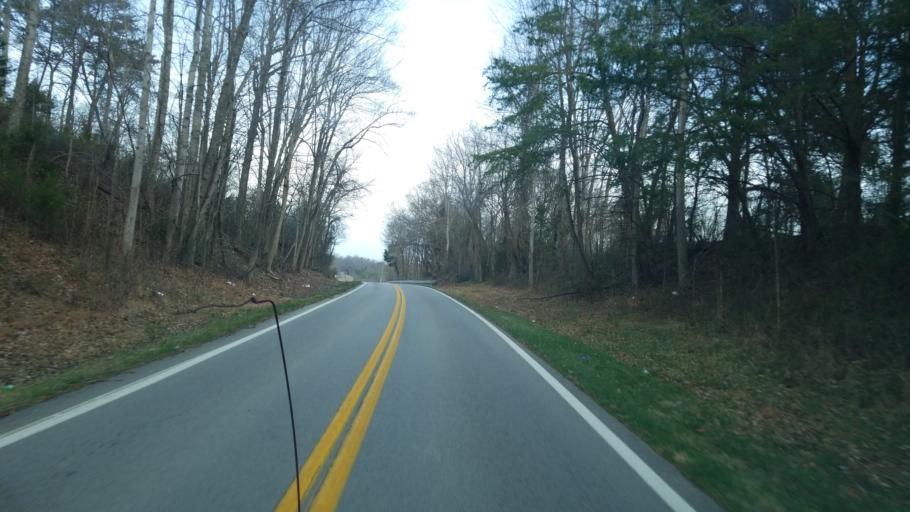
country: US
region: Kentucky
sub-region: Clinton County
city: Albany
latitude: 36.8189
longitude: -85.1839
